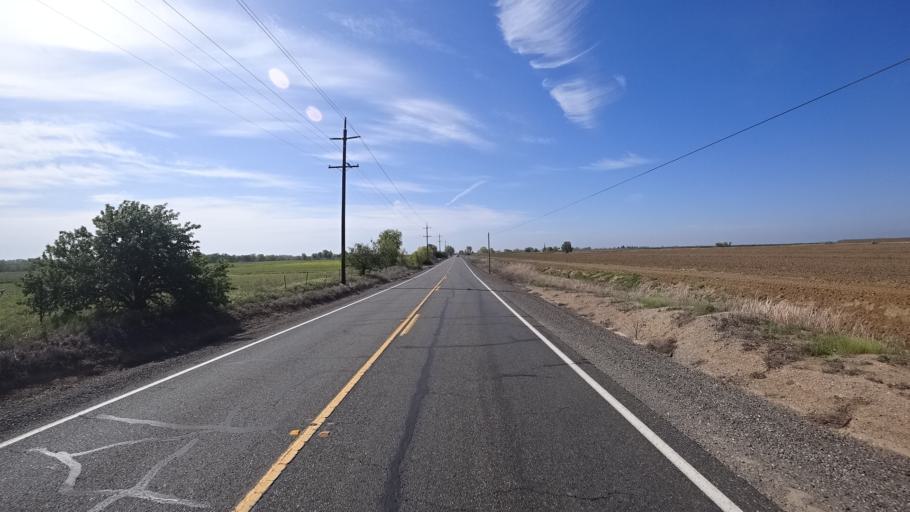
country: US
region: California
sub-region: Glenn County
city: Hamilton City
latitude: 39.6813
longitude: -122.0052
